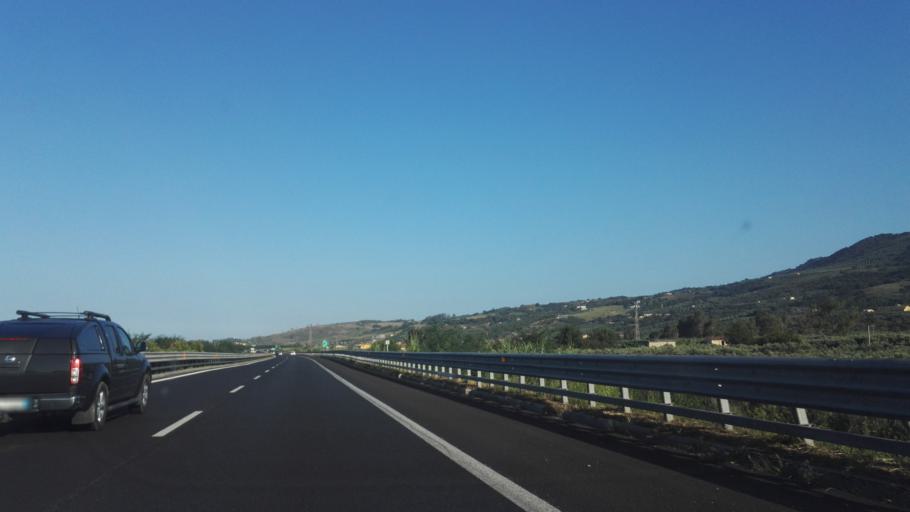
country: IT
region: Calabria
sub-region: Provincia di Catanzaro
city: Gizzeria
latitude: 38.9396
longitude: 16.2045
